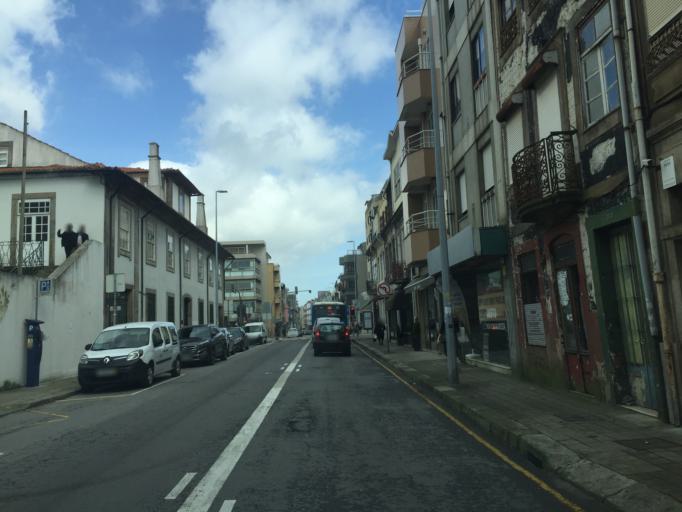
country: PT
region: Porto
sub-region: Porto
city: Porto
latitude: 41.1610
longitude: -8.6115
